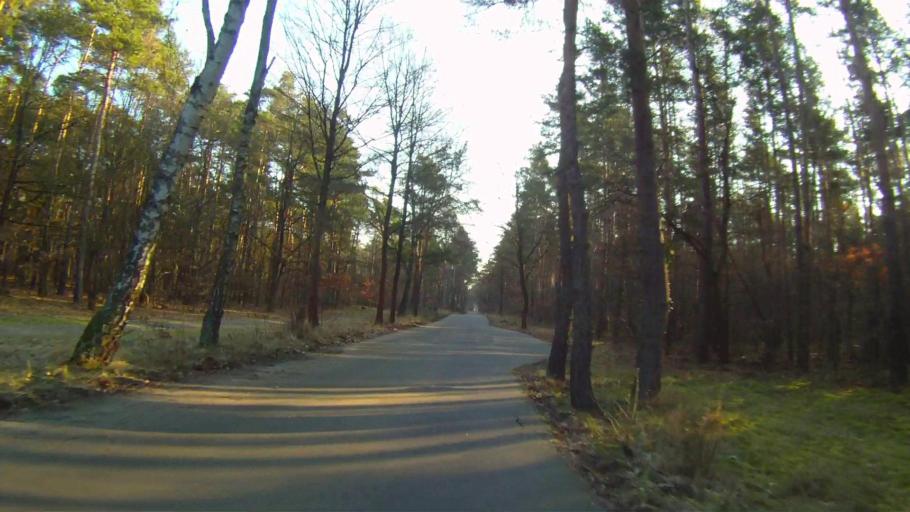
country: DE
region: Berlin
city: Friedrichshagen
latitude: 52.4423
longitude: 13.6105
